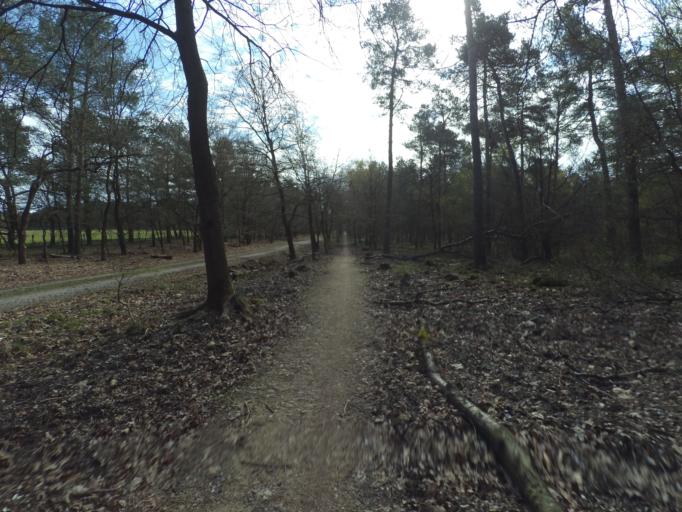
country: NL
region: Gelderland
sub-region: Gemeente Apeldoorn
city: Uddel
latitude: 52.3108
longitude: 5.7803
